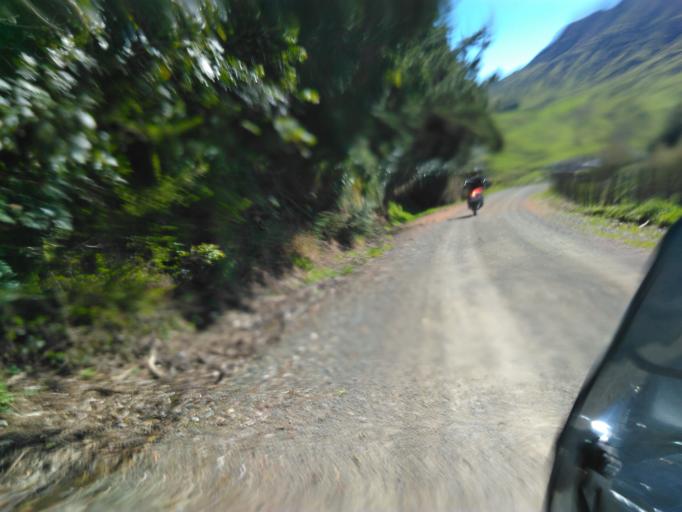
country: NZ
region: Bay of Plenty
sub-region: Opotiki District
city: Opotiki
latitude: -38.3478
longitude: 177.5844
